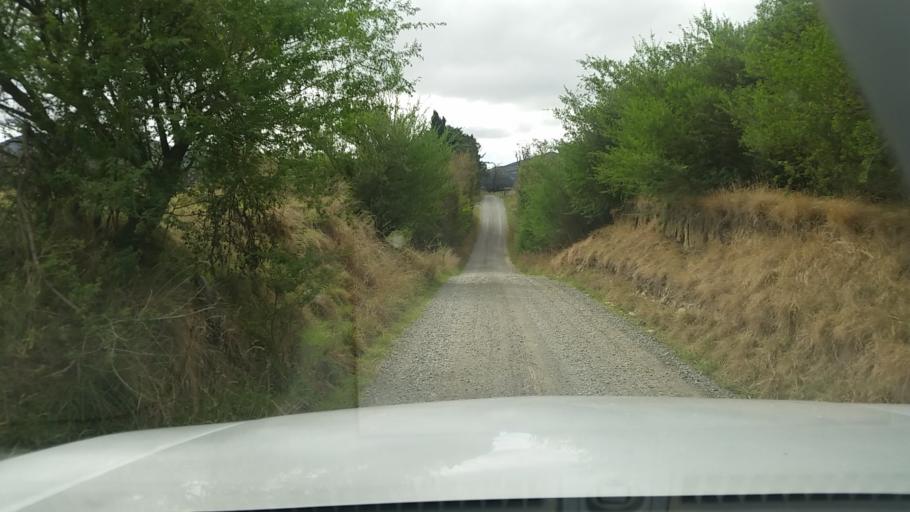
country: NZ
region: Marlborough
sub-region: Marlborough District
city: Blenheim
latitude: -41.6721
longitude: 174.0386
